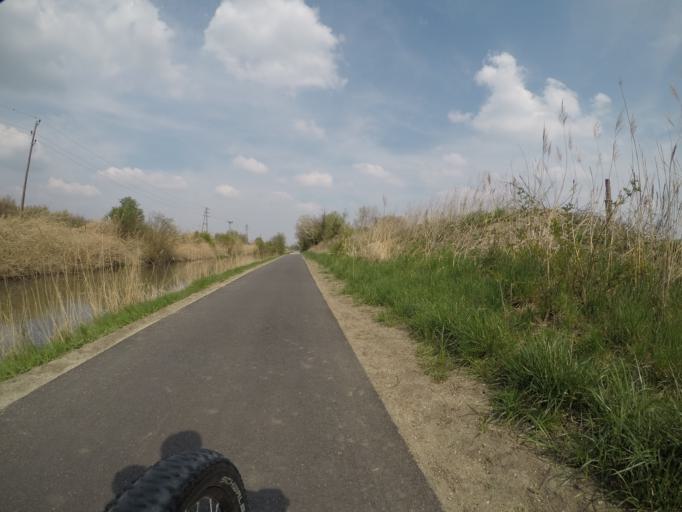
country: AT
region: Lower Austria
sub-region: Politischer Bezirk Baden
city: Pfaffstatten
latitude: 48.0228
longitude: 16.2787
